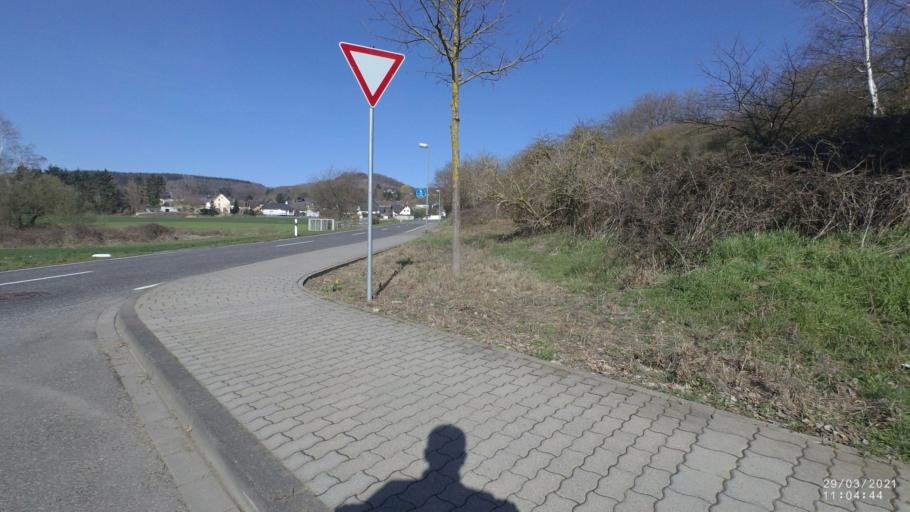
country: DE
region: Rheinland-Pfalz
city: Kretz
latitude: 50.4237
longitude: 7.3573
